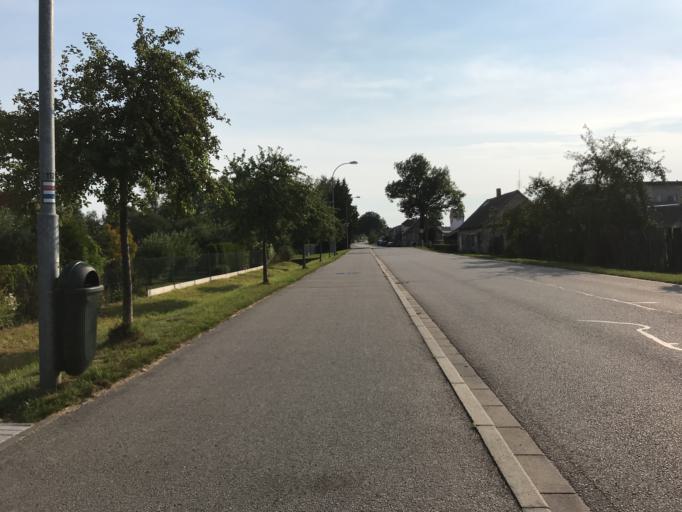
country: CZ
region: Jihocesky
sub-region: Okres Jindrichuv Hradec
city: Trebon
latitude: 49.0078
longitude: 14.7793
